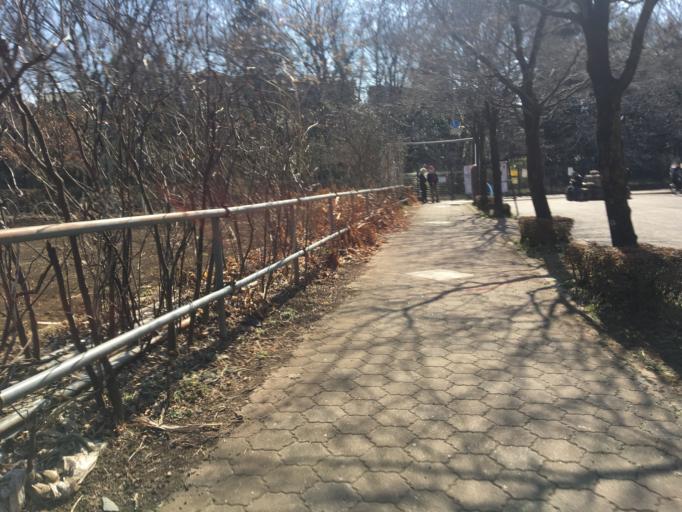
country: JP
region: Saitama
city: Oi
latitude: 35.8514
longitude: 139.5228
